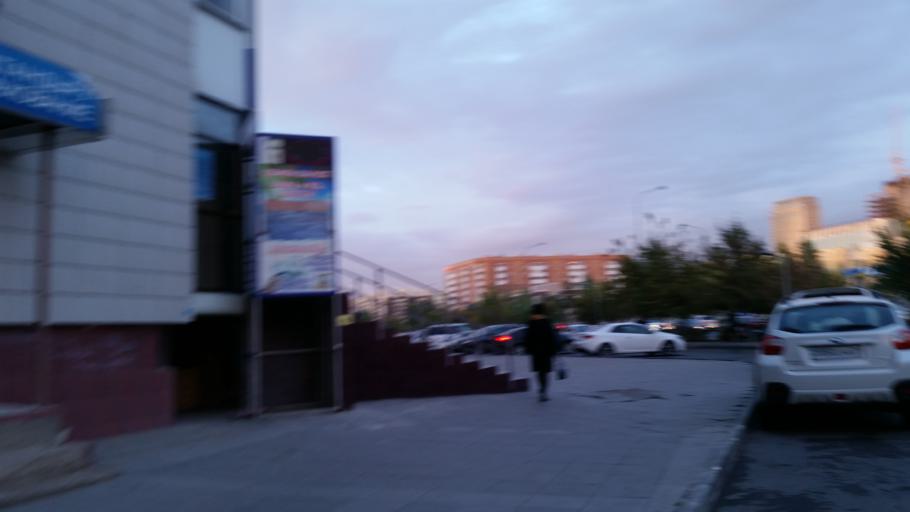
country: KZ
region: Astana Qalasy
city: Astana
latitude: 51.1204
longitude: 71.4199
